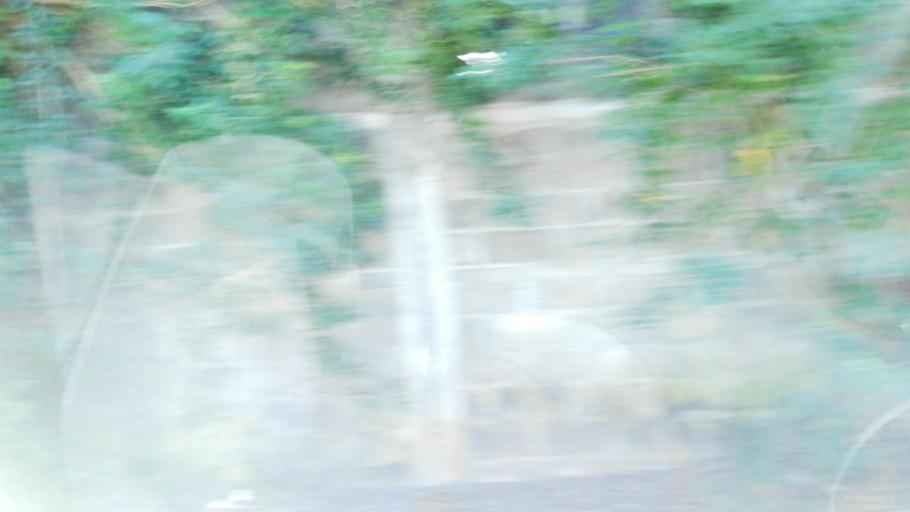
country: MU
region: Plaines Wilhems
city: Ebene
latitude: -20.2294
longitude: 57.4736
